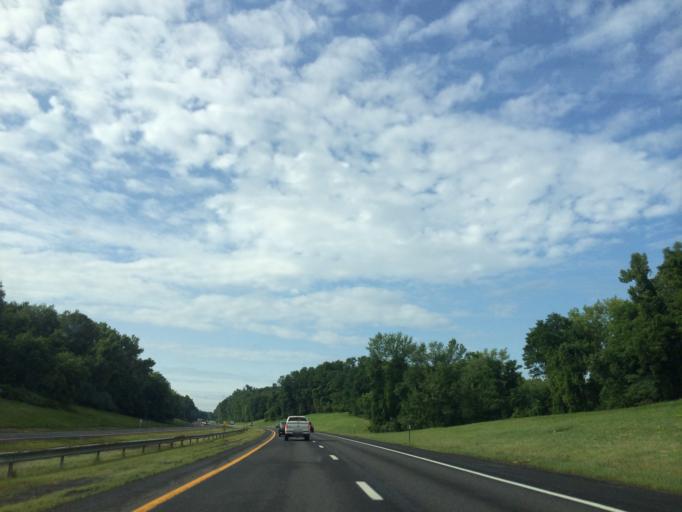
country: US
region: New York
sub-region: Ulster County
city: Rosendale Village
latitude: 41.8496
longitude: -74.0600
